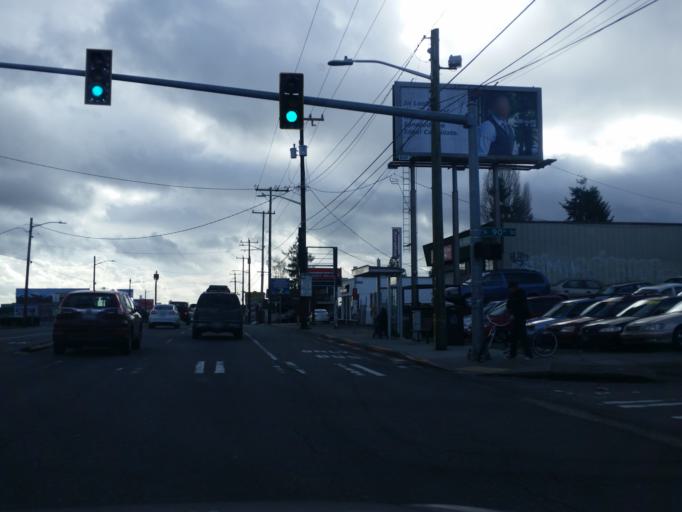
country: US
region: Washington
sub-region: King County
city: Shoreline
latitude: 47.6943
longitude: -122.3447
